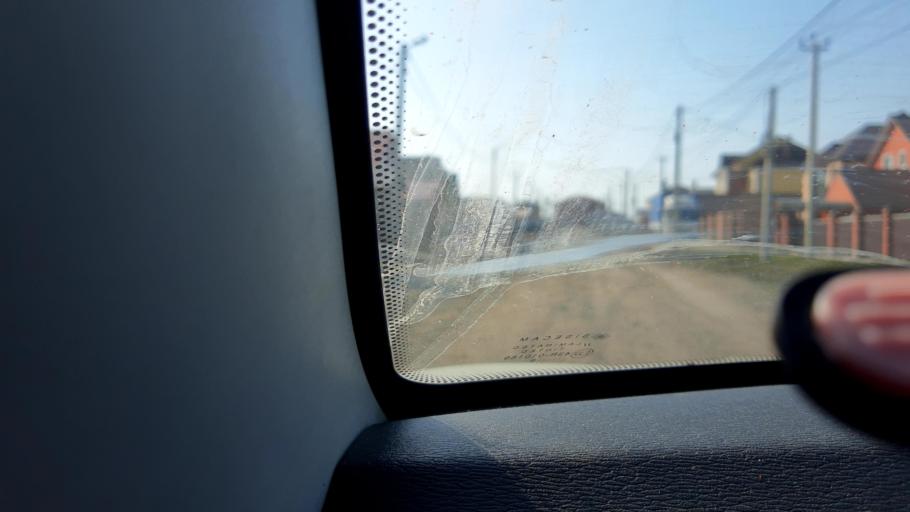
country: RU
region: Bashkortostan
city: Kabakovo
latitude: 54.6140
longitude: 56.0941
